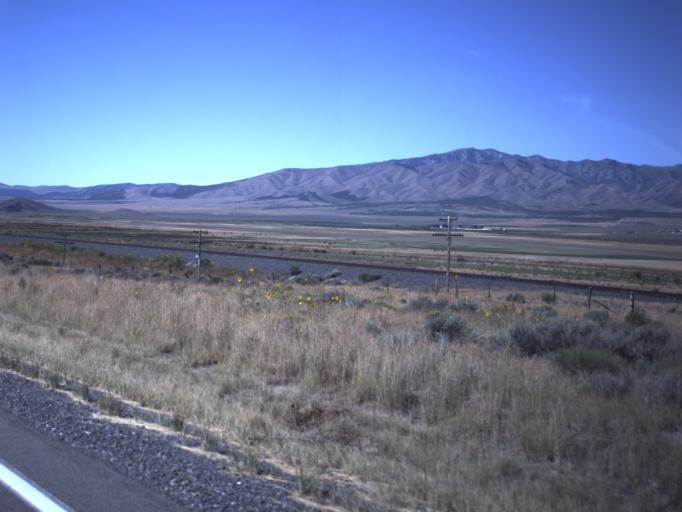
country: US
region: Utah
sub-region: Tooele County
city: Tooele
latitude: 40.4336
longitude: -112.3762
